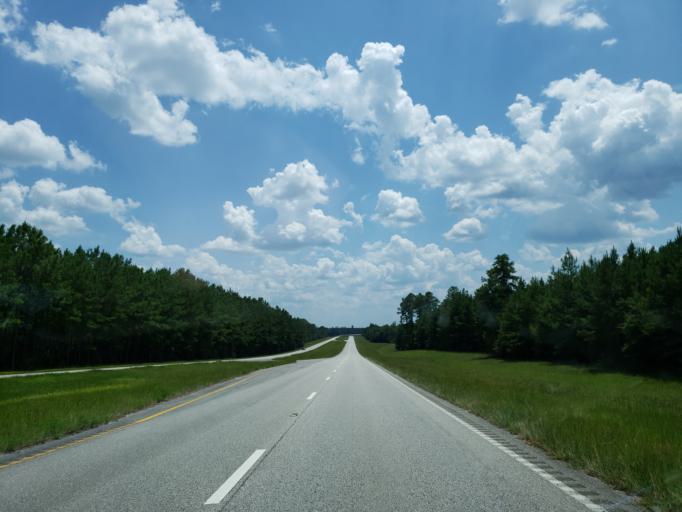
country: US
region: Mississippi
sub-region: Greene County
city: Leakesville
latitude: 31.3071
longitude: -88.4998
